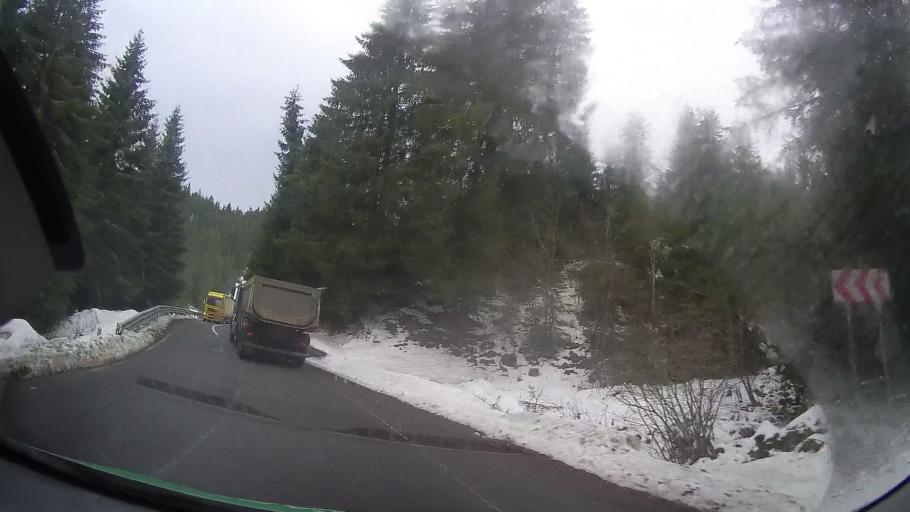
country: RO
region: Harghita
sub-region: Municipiul Gheorgheni
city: Gheorgheni
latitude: 46.7797
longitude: 25.7219
